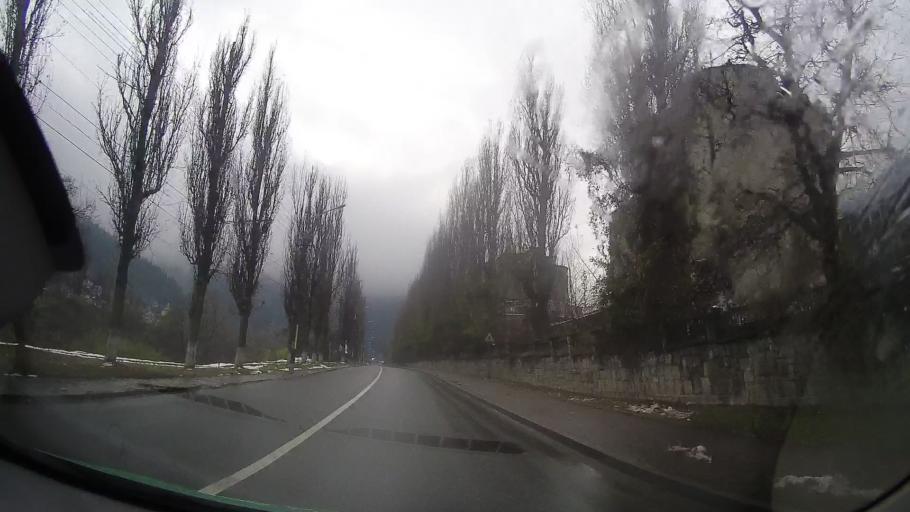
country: RO
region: Neamt
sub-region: Comuna Bicaz
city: Bicaz
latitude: 46.9056
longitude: 26.0761
